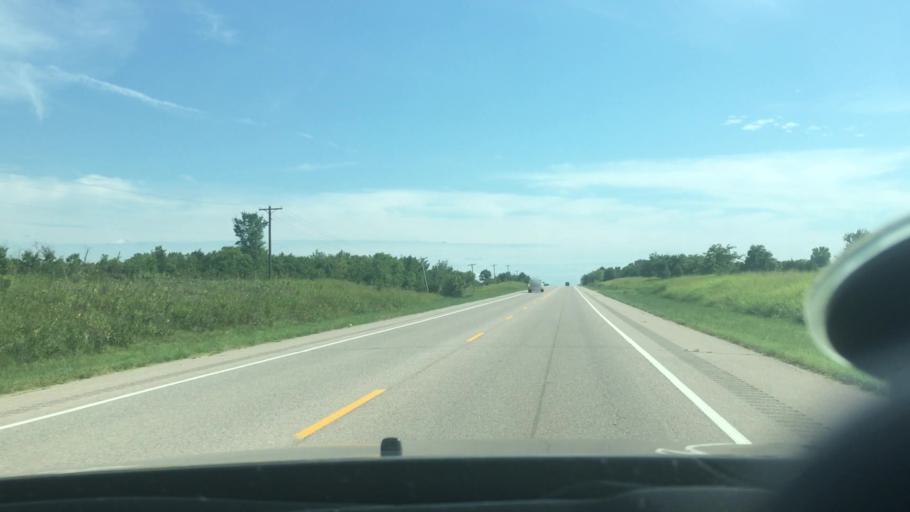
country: US
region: Oklahoma
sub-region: Seminole County
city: Konawa
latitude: 34.9802
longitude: -96.6793
